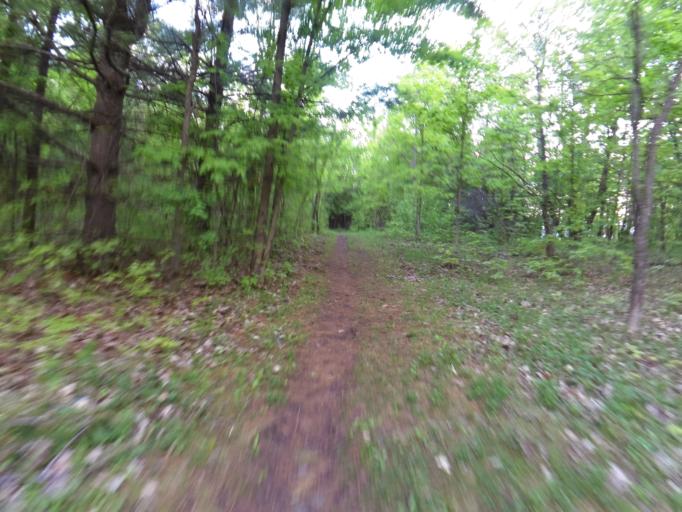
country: CA
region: Ontario
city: Bells Corners
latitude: 45.3175
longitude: -75.8590
